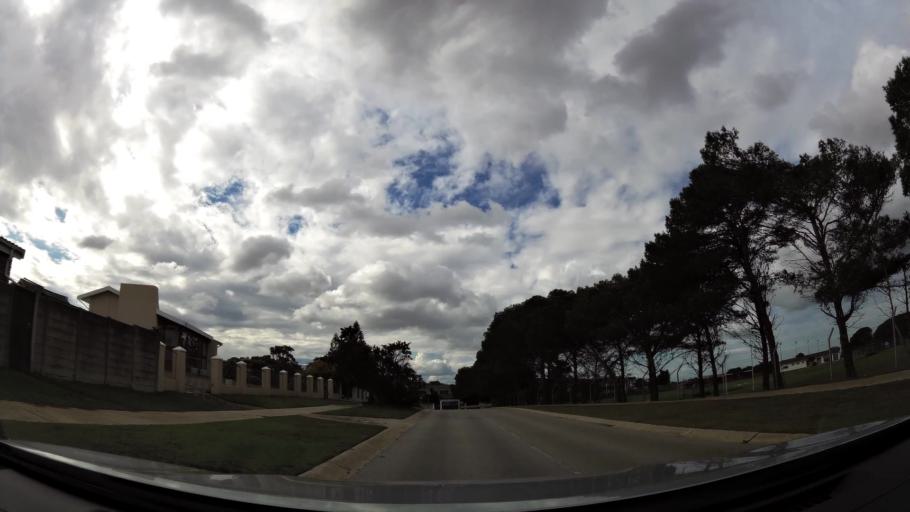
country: ZA
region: Eastern Cape
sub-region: Nelson Mandela Bay Metropolitan Municipality
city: Port Elizabeth
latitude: -33.9338
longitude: 25.5261
